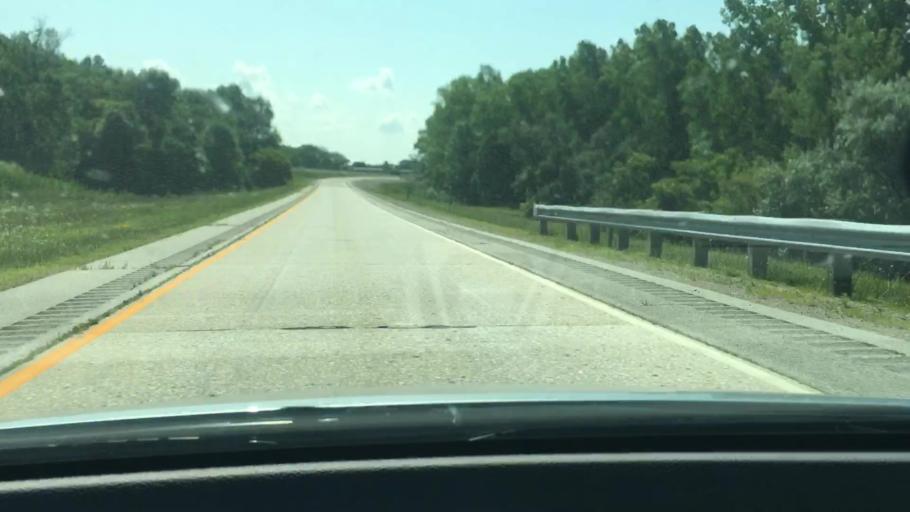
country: US
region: Wisconsin
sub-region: Brown County
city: Ashwaubenon
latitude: 44.4838
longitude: -88.0836
